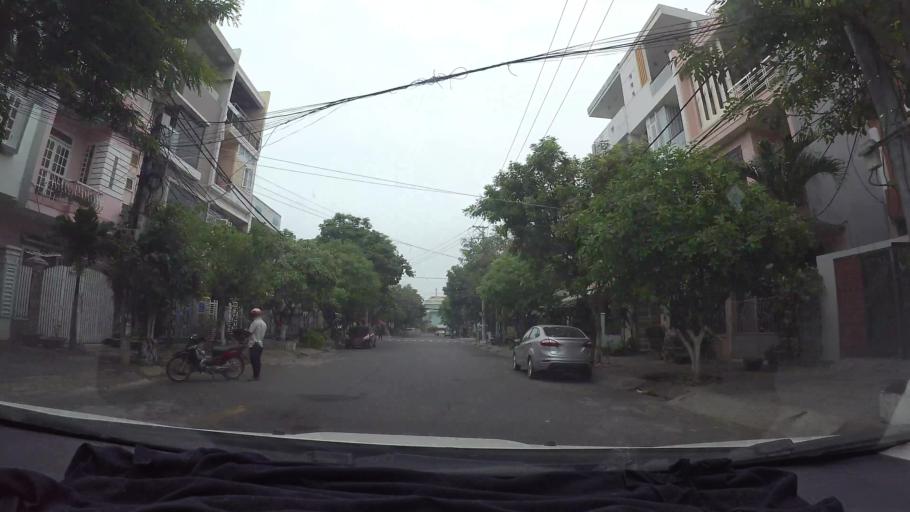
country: VN
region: Da Nang
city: Cam Le
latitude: 16.0341
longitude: 108.2205
